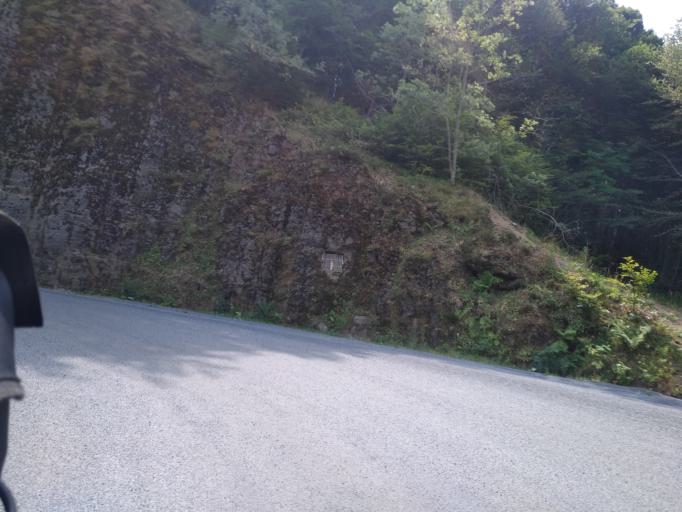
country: FR
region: Auvergne
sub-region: Departement du Cantal
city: Riom-es-Montagnes
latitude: 45.1274
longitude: 2.6971
